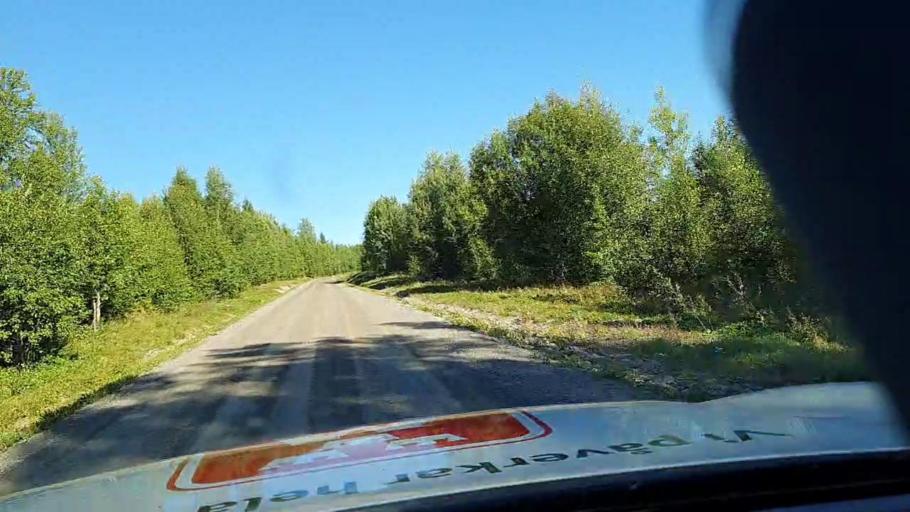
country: SE
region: Jaemtland
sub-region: Stroemsunds Kommun
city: Stroemsund
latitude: 64.0170
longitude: 15.9324
